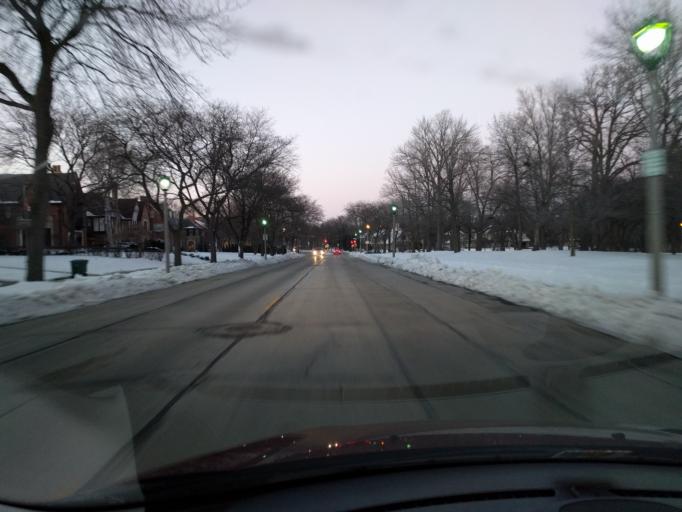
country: US
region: Wisconsin
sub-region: Milwaukee County
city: Shorewood
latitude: 43.0731
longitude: -87.8721
